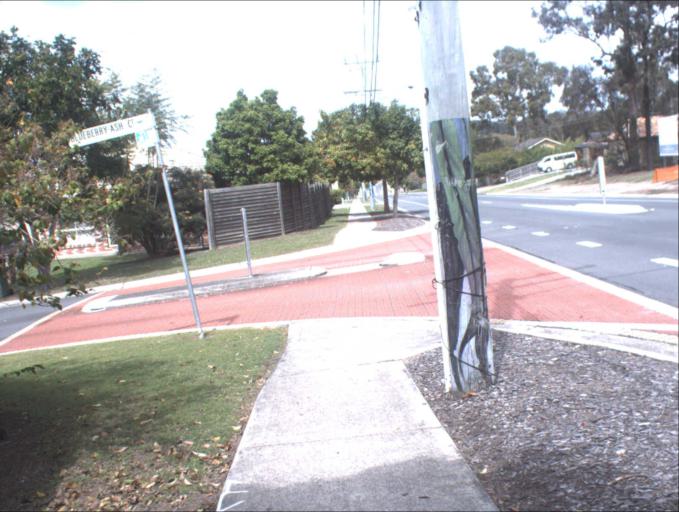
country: AU
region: Queensland
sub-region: Logan
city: Park Ridge South
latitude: -27.6881
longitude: 153.0228
